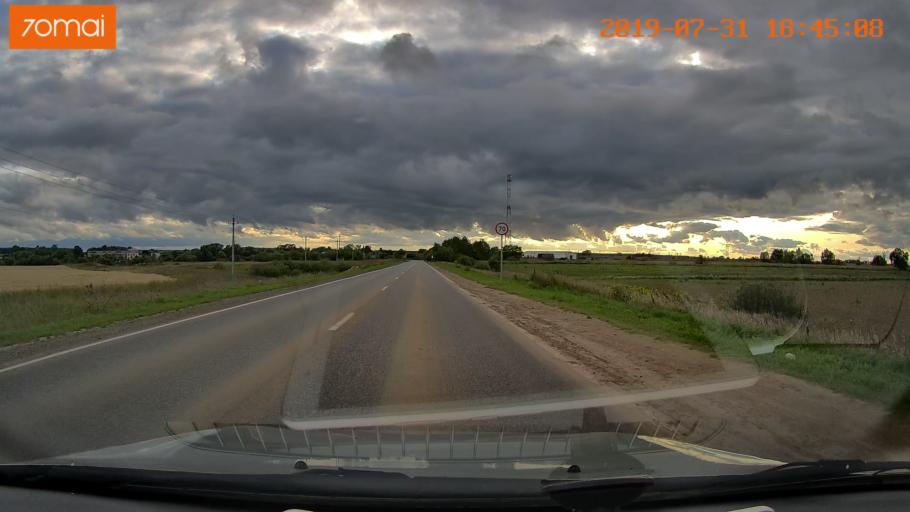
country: RU
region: Moskovskaya
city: Troitskoye
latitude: 55.2519
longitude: 38.5377
